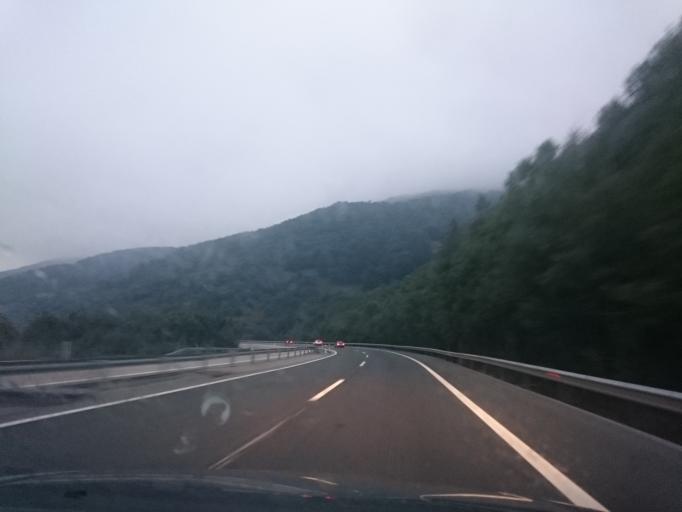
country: ES
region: Asturias
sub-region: Province of Asturias
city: Pola de Lena
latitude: 43.0384
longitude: -5.8210
